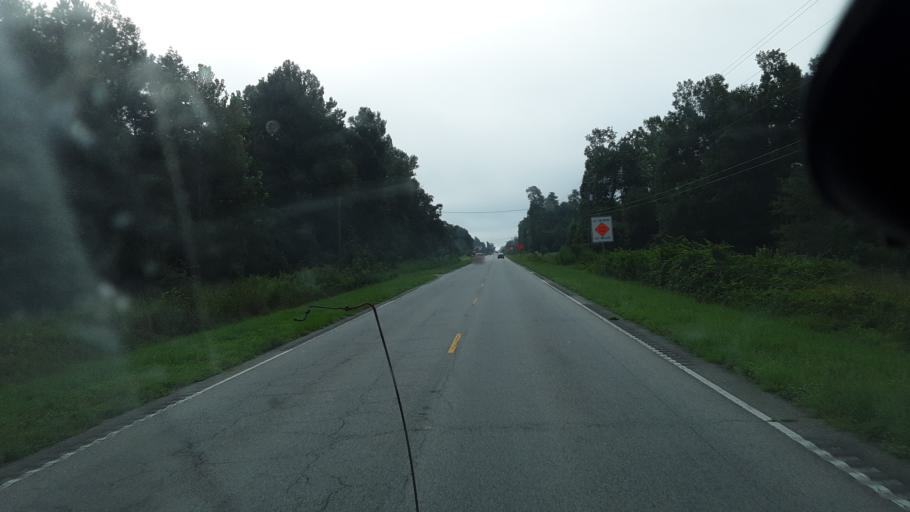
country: US
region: South Carolina
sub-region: Florence County
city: Johnsonville
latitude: 33.8682
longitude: -79.3399
